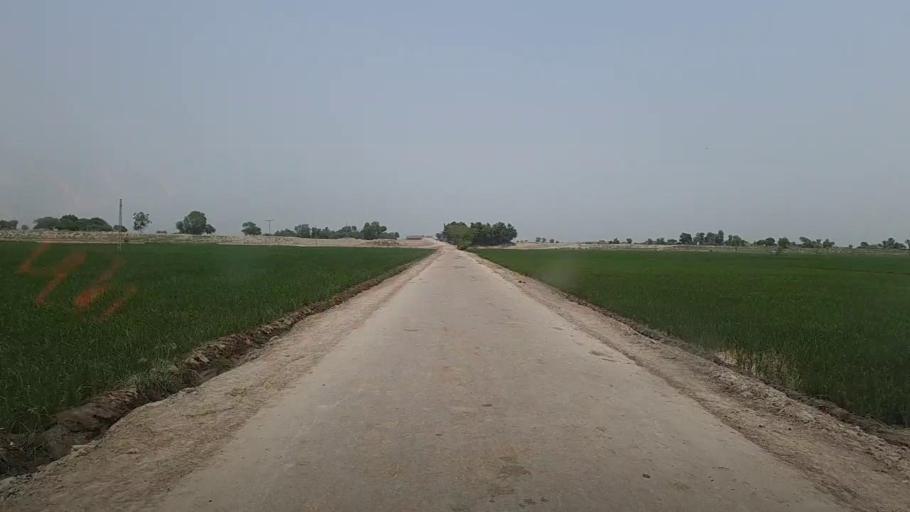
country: PK
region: Sindh
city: Sita Road
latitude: 27.0479
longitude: 67.8472
